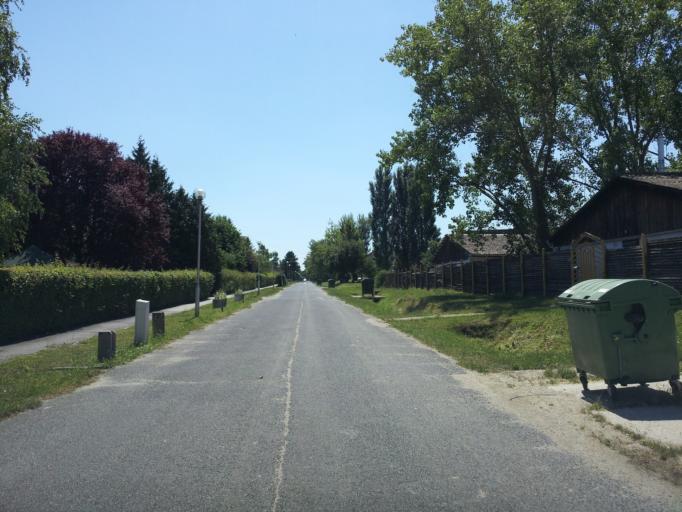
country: HU
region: Veszprem
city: Berhida
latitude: 47.1218
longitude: 18.1089
